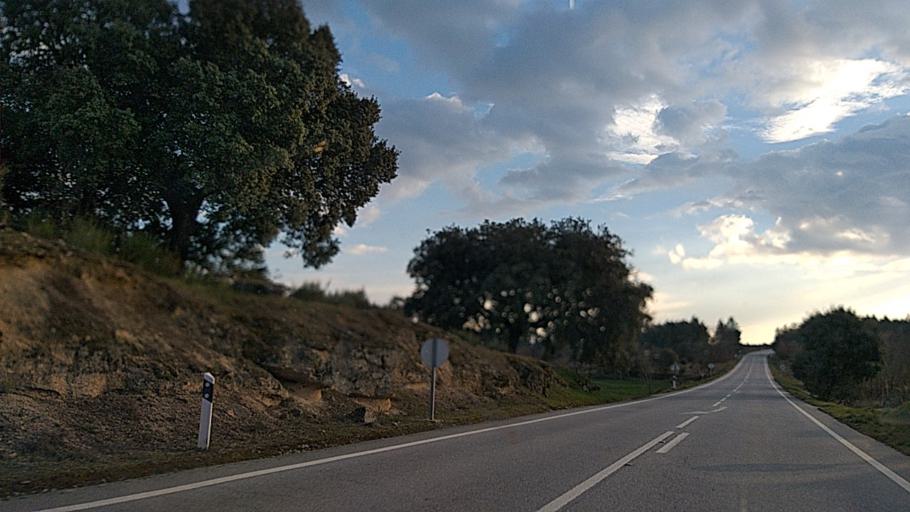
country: PT
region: Guarda
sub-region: Pinhel
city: Pinhel
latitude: 40.6728
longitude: -6.9518
